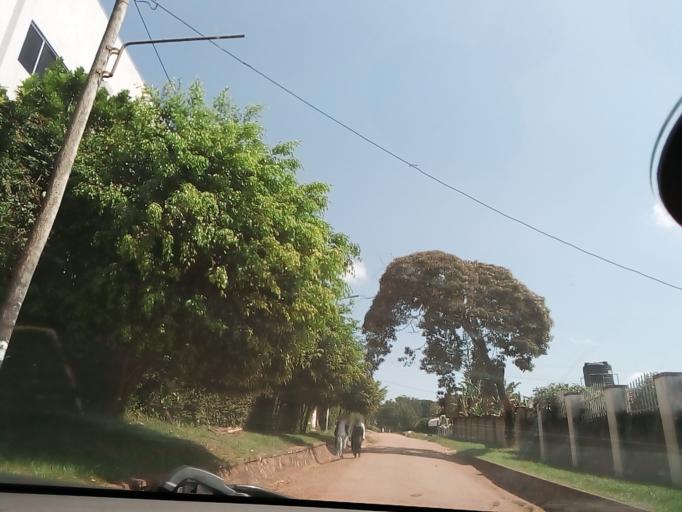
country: UG
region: Central Region
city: Masaka
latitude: -0.3330
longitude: 31.7408
